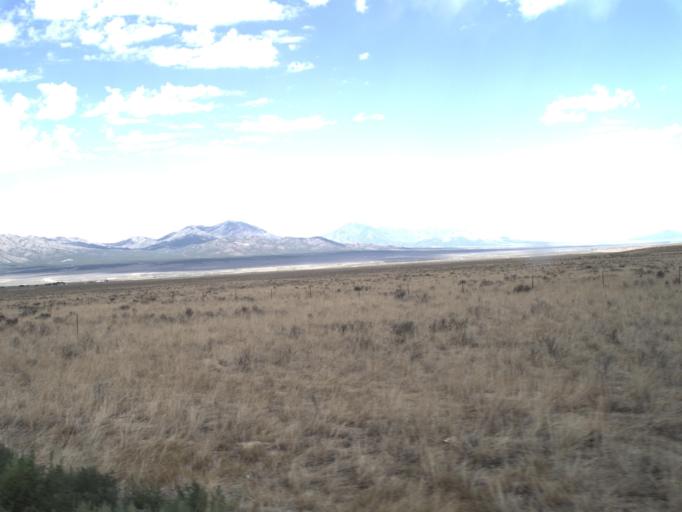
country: US
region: Utah
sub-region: Utah County
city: Eagle Mountain
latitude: 40.0807
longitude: -112.4051
